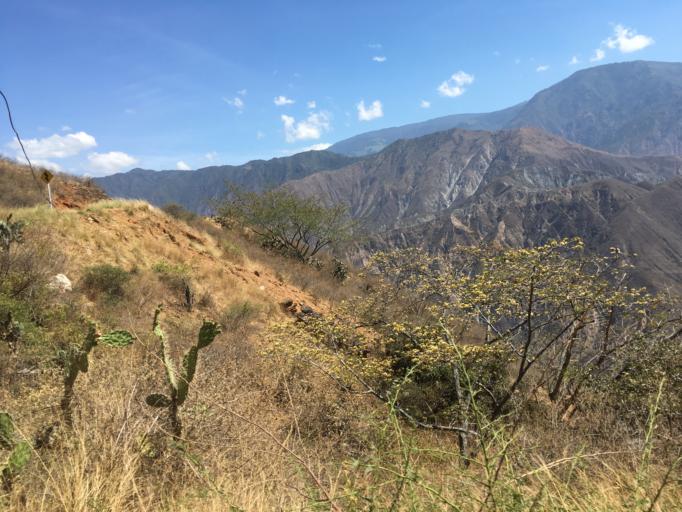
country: CO
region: Santander
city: Aratoca
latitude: 6.7871
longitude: -72.9962
